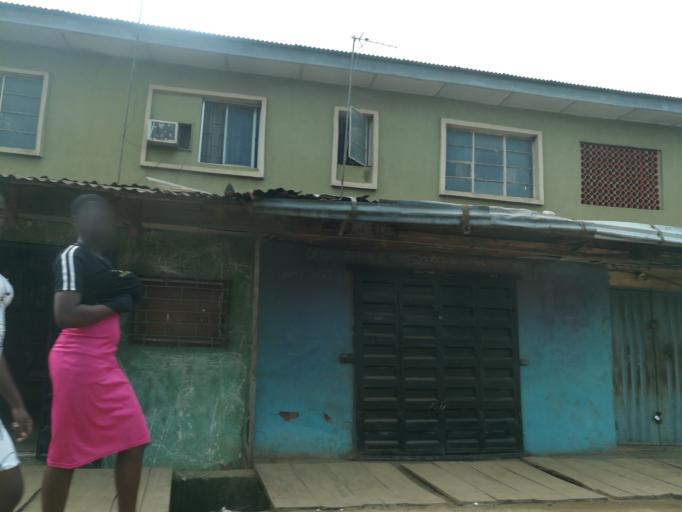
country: NG
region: Lagos
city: Ikorodu
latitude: 6.6200
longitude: 3.5084
